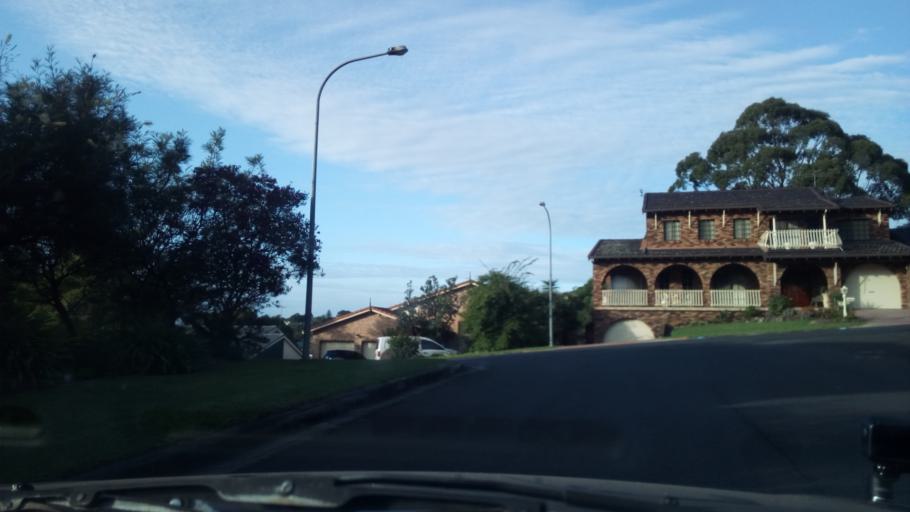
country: AU
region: New South Wales
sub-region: Wollongong
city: Mount Ousley
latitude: -34.3836
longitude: 150.8711
